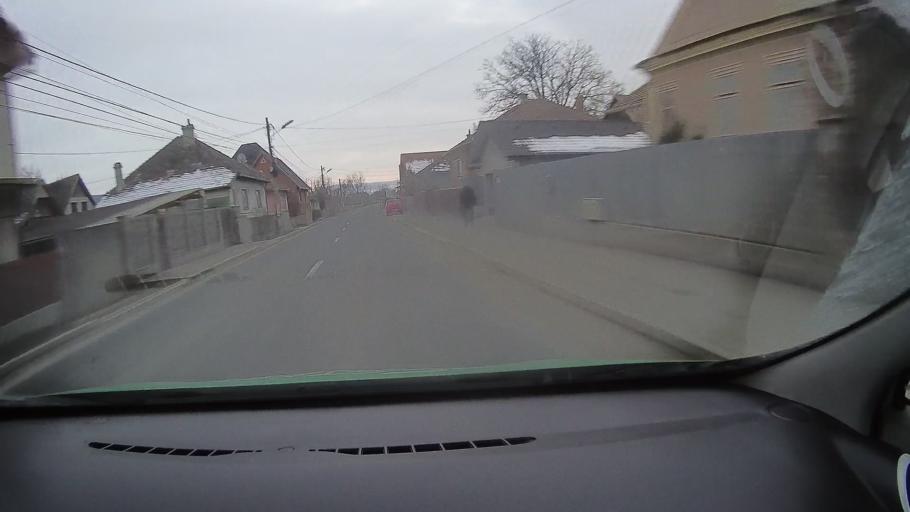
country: RO
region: Harghita
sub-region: Municipiul Odorheiu Secuiesc
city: Odorheiu Secuiesc
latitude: 46.3076
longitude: 25.2858
